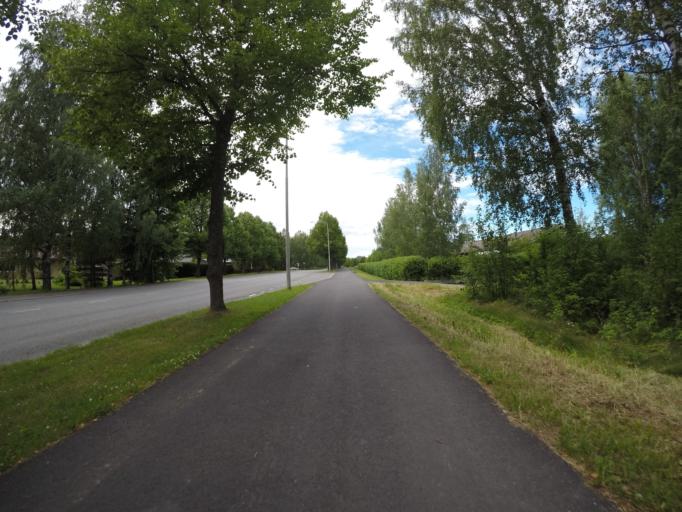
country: FI
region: Haeme
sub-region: Haemeenlinna
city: Haemeenlinna
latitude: 61.0070
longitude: 24.4108
